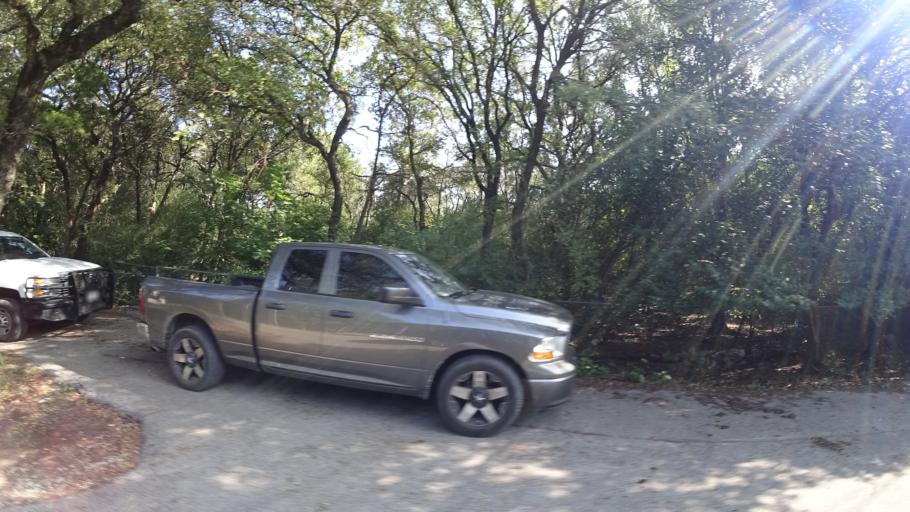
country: US
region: Texas
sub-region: Travis County
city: West Lake Hills
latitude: 30.2881
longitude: -97.8009
